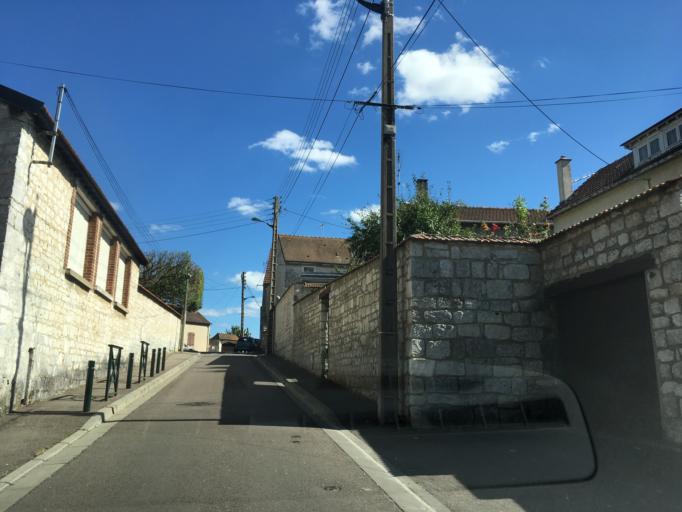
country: FR
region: Haute-Normandie
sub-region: Departement de l'Eure
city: Vernon
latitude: 49.0845
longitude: 1.4948
